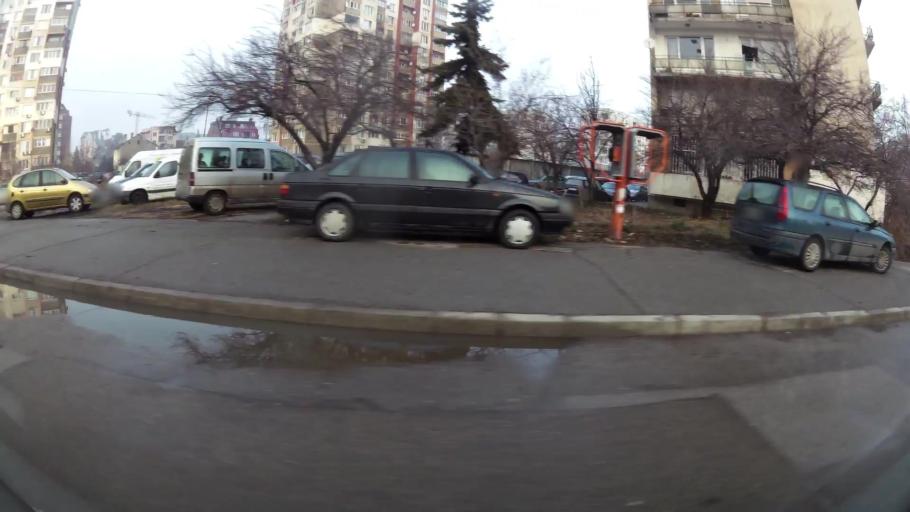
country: BG
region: Sofia-Capital
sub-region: Stolichna Obshtina
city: Sofia
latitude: 42.7312
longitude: 23.3069
